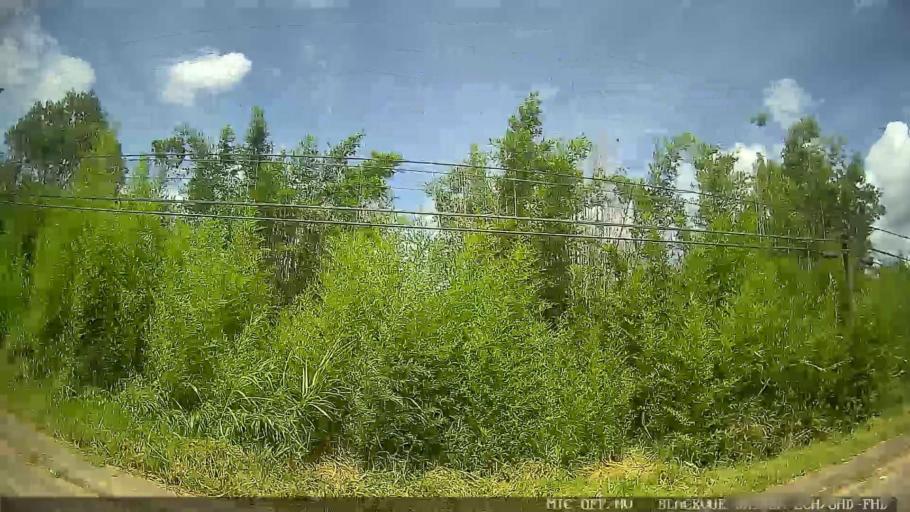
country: BR
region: Sao Paulo
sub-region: Suzano
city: Suzano
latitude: -23.6556
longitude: -46.2367
